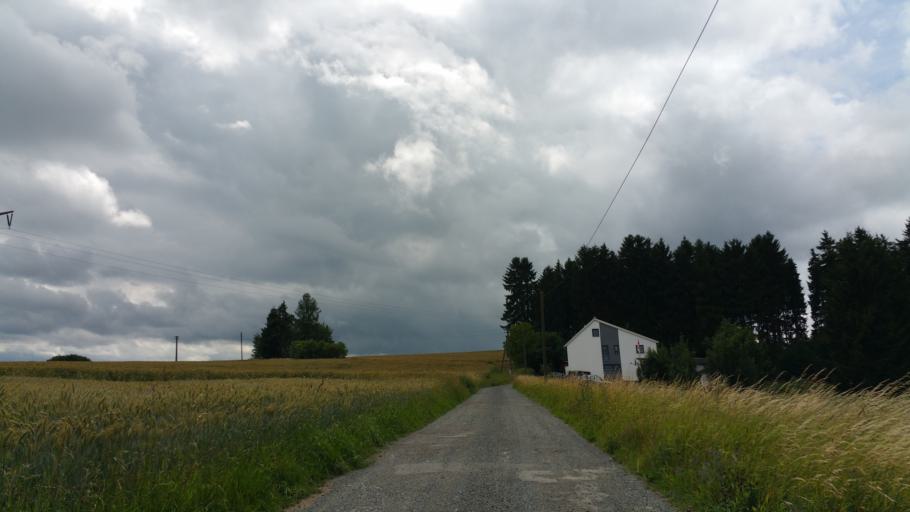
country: DE
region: Bavaria
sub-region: Upper Franconia
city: Rehau
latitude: 50.2613
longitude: 12.0392
